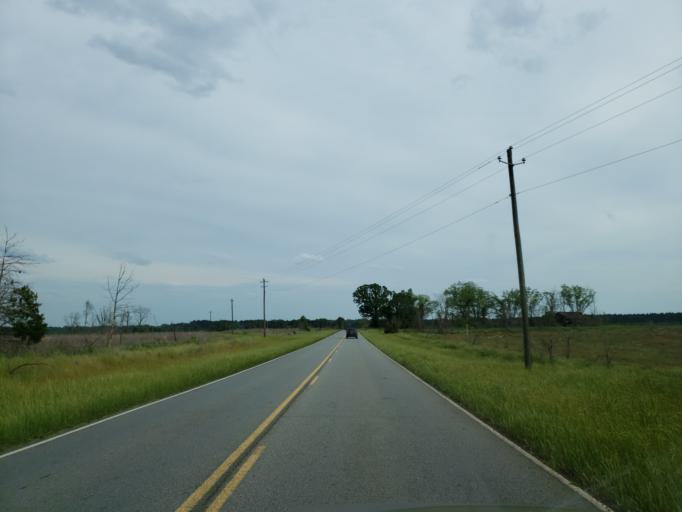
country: US
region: Georgia
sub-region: Macon County
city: Montezuma
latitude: 32.2177
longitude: -83.9333
